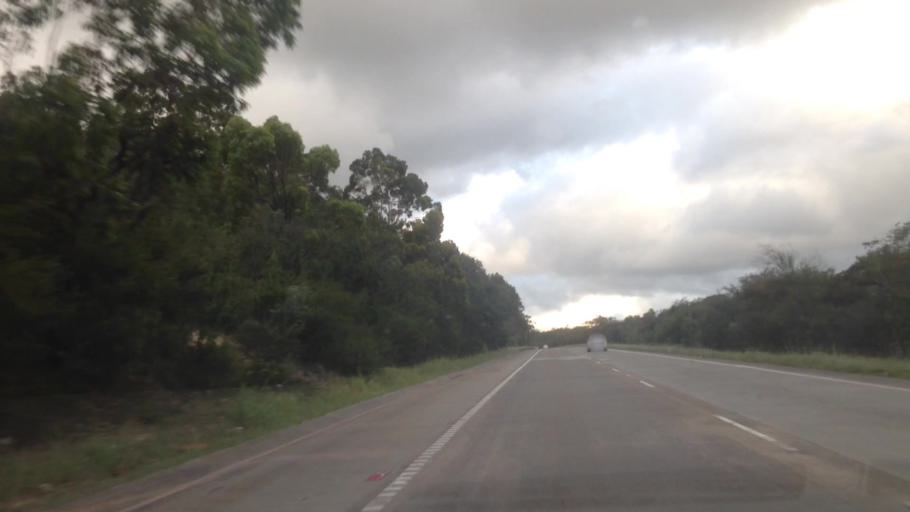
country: AU
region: New South Wales
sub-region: Wyong Shire
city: Jilliby
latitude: -33.2047
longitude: 151.4580
